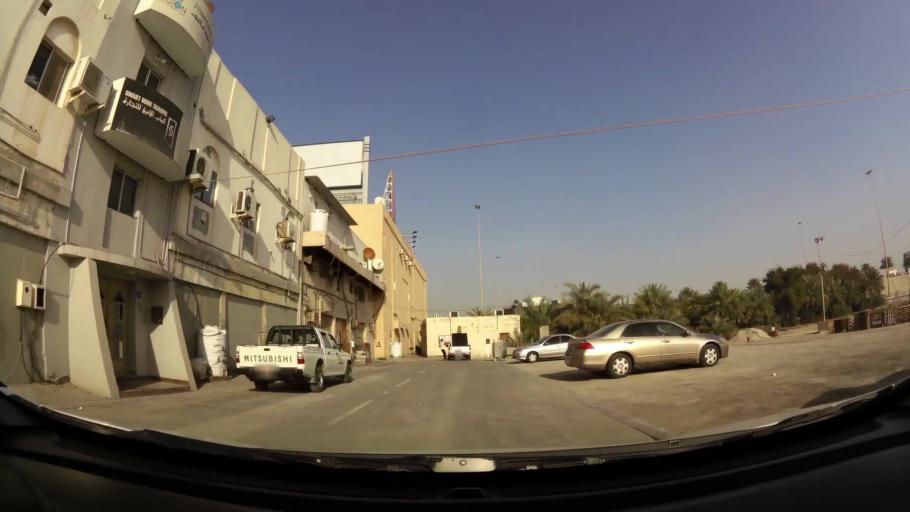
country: BH
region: Manama
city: Jidd Hafs
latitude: 26.2174
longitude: 50.5197
